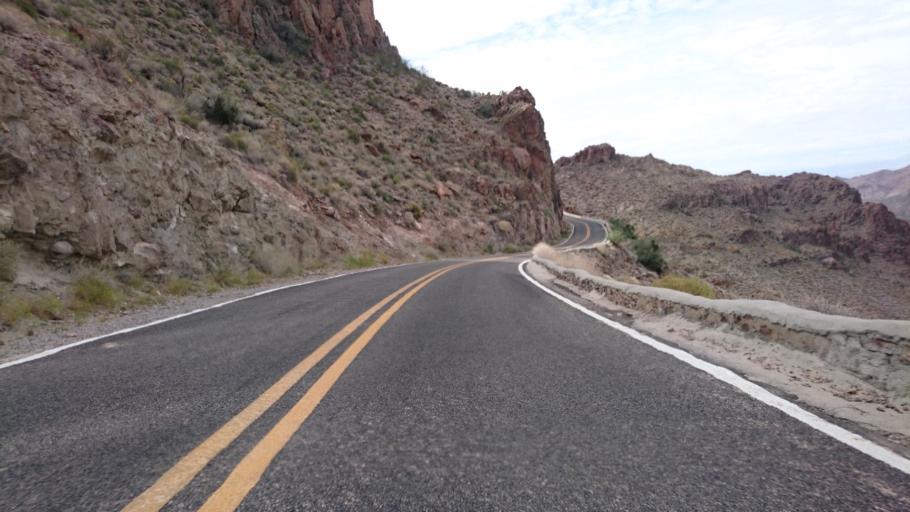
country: US
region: Arizona
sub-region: Mohave County
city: Bullhead City
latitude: 35.0446
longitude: -114.3659
